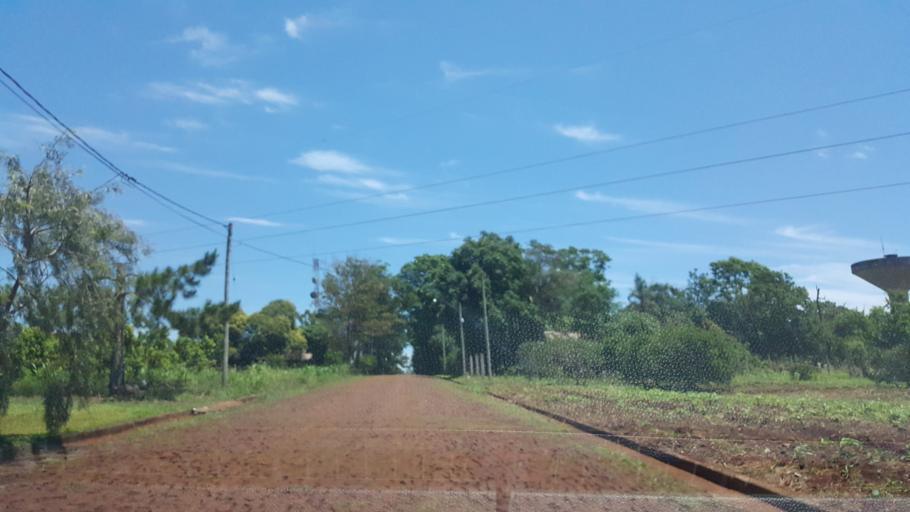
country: AR
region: Misiones
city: Capiovi
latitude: -26.9360
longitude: -55.0562
